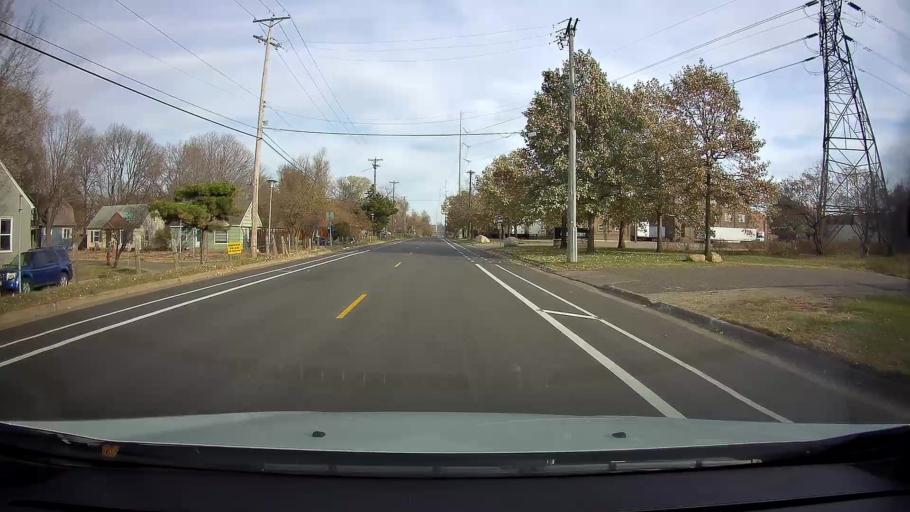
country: US
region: Minnesota
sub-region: Ramsey County
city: Lauderdale
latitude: 44.9842
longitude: -93.2220
